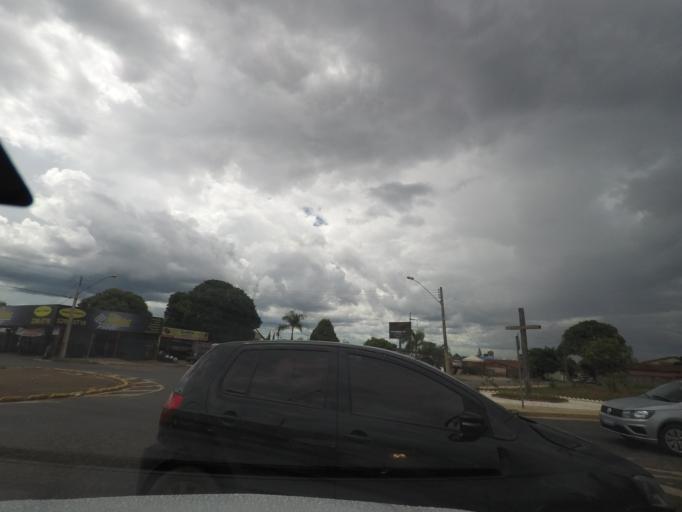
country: BR
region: Goias
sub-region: Goiania
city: Goiania
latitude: -16.7373
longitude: -49.3262
